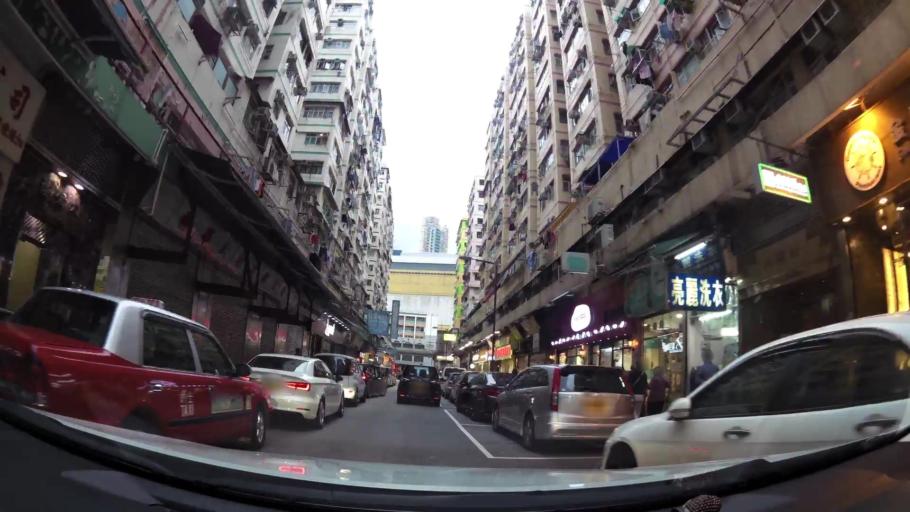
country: HK
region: Sham Shui Po
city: Sham Shui Po
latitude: 22.3218
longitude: 114.1606
